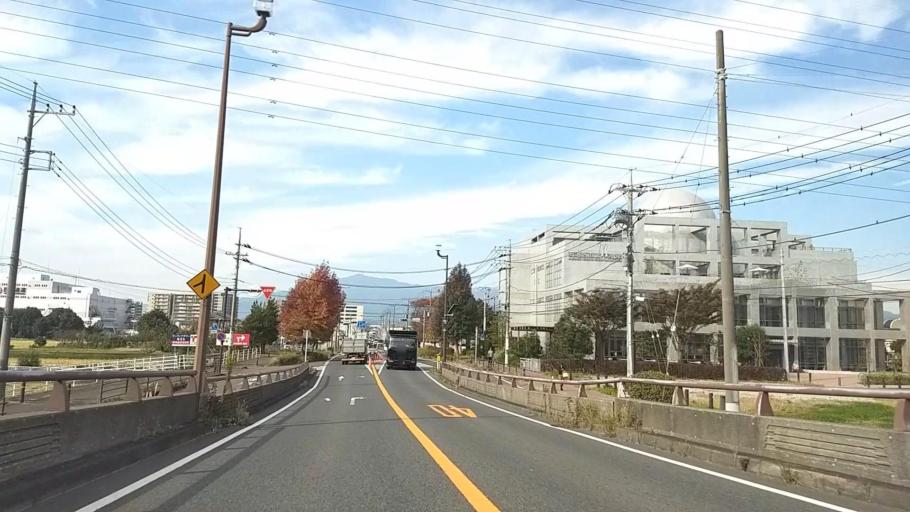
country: JP
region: Kanagawa
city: Atsugi
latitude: 35.4510
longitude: 139.3875
